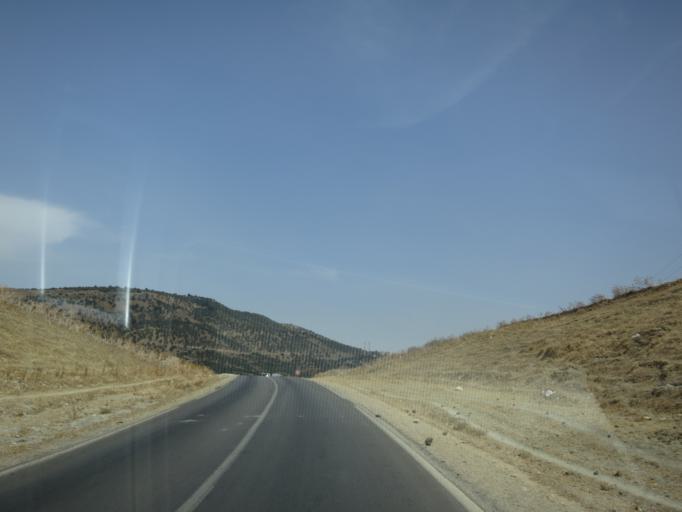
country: MA
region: Meknes-Tafilalet
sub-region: Meknes
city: Meknes
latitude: 34.0514
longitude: -5.5405
